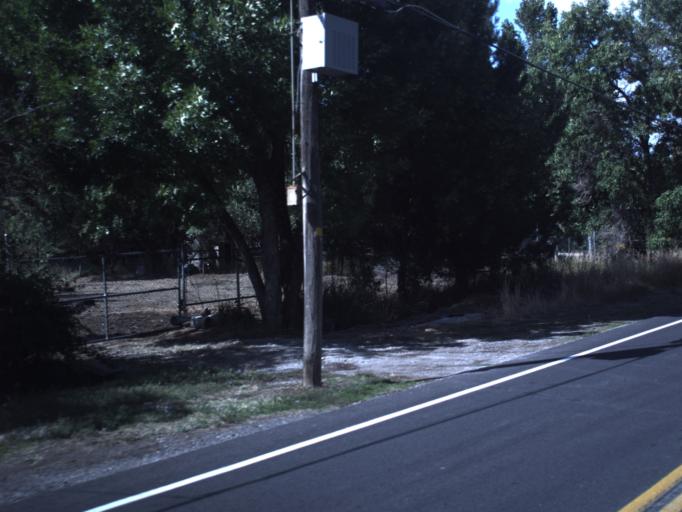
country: US
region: Utah
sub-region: Utah County
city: Mapleton
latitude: 40.1210
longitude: -111.5787
